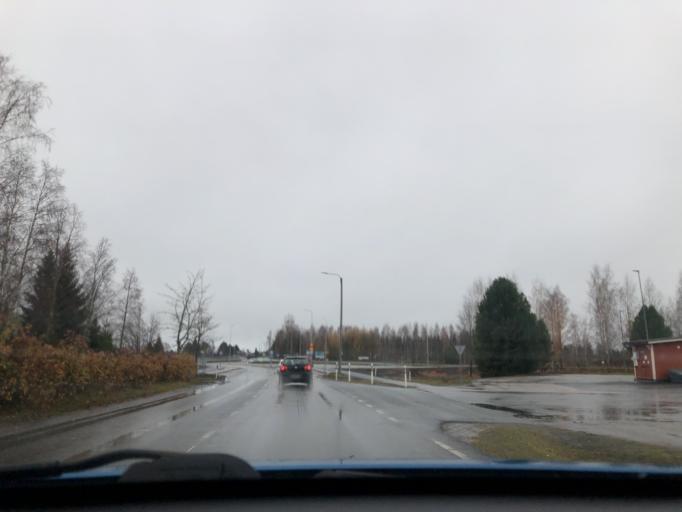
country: FI
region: Pirkanmaa
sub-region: Tampere
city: Kangasala
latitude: 61.4666
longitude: 24.0384
